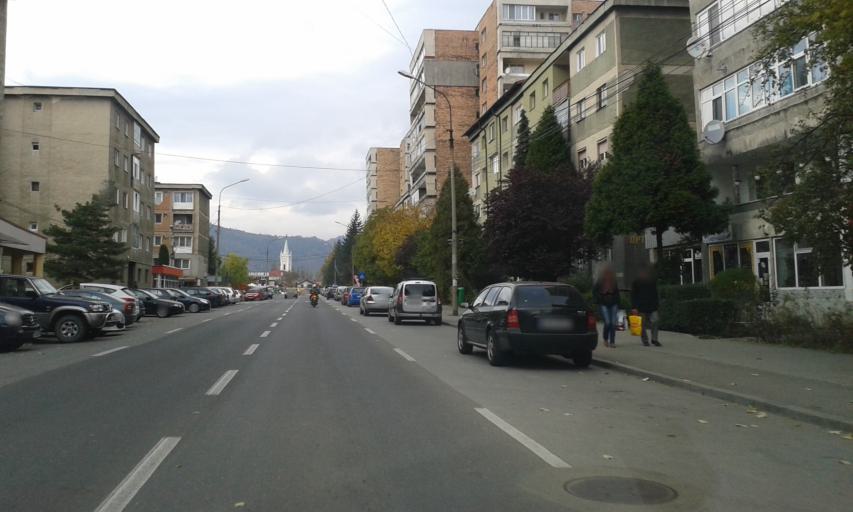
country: RO
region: Hunedoara
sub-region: Municipiul Petrosani
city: Petrosani
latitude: 45.4139
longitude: 23.3714
